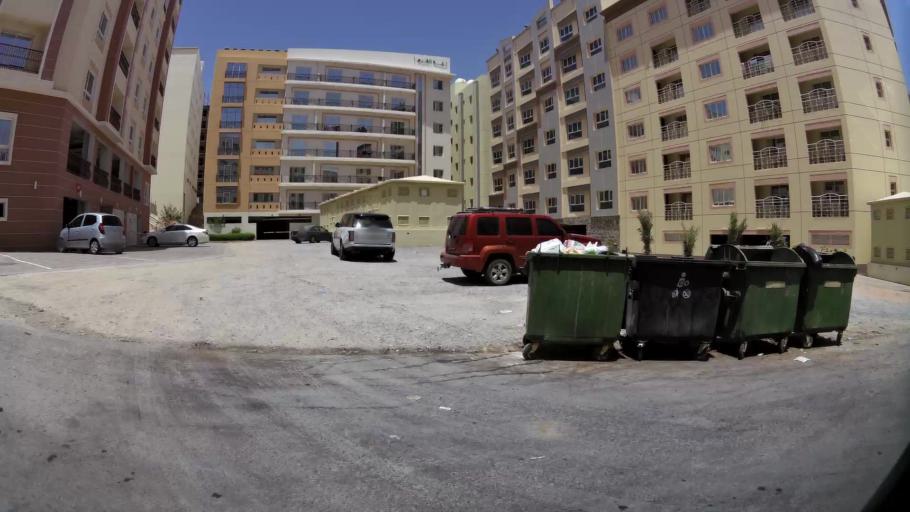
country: OM
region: Muhafazat Masqat
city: Muscat
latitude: 23.6214
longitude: 58.5011
